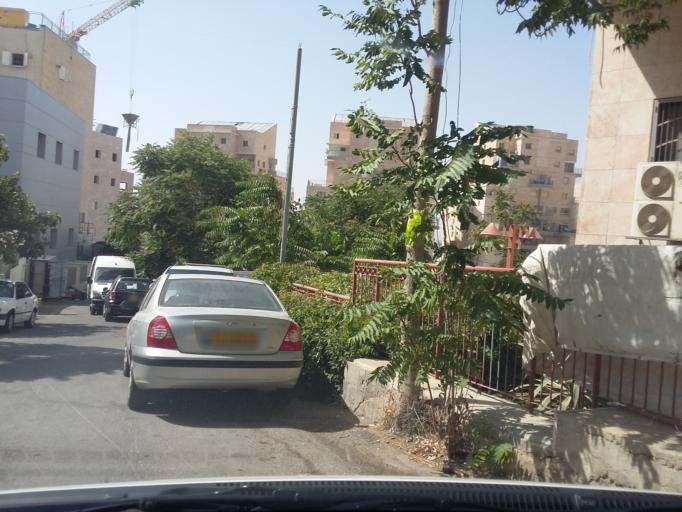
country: IL
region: Jerusalem
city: West Jerusalem
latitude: 31.7919
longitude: 35.2035
